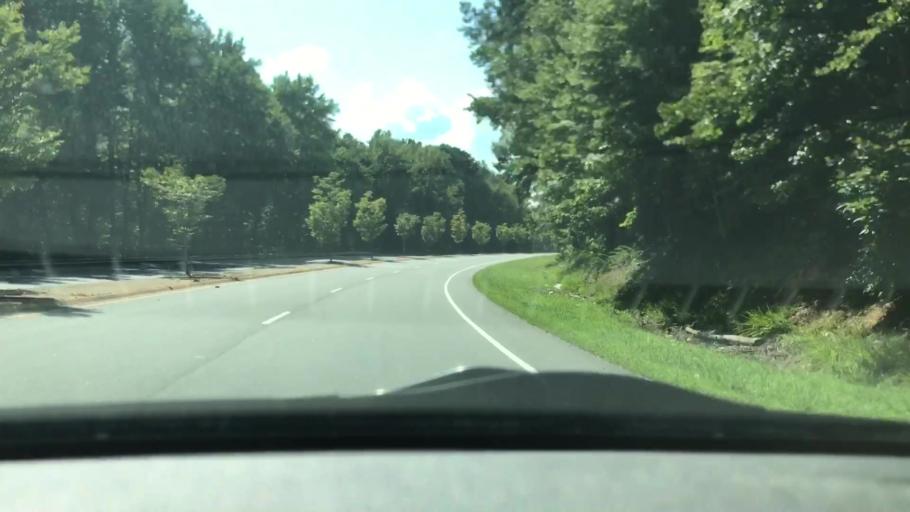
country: US
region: North Carolina
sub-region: Randolph County
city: Asheboro
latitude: 35.7354
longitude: -79.8124
